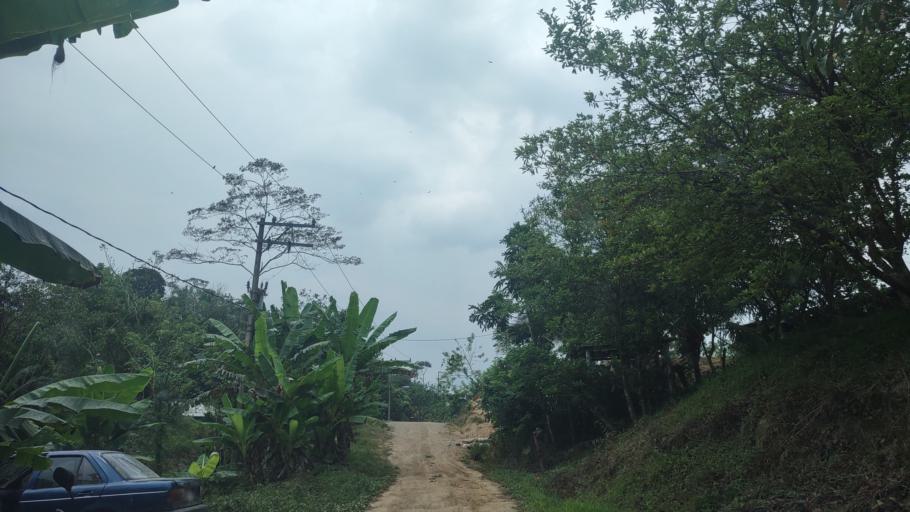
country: MX
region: Veracruz
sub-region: Uxpanapa
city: Poblado 10
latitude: 17.4536
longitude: -94.1001
